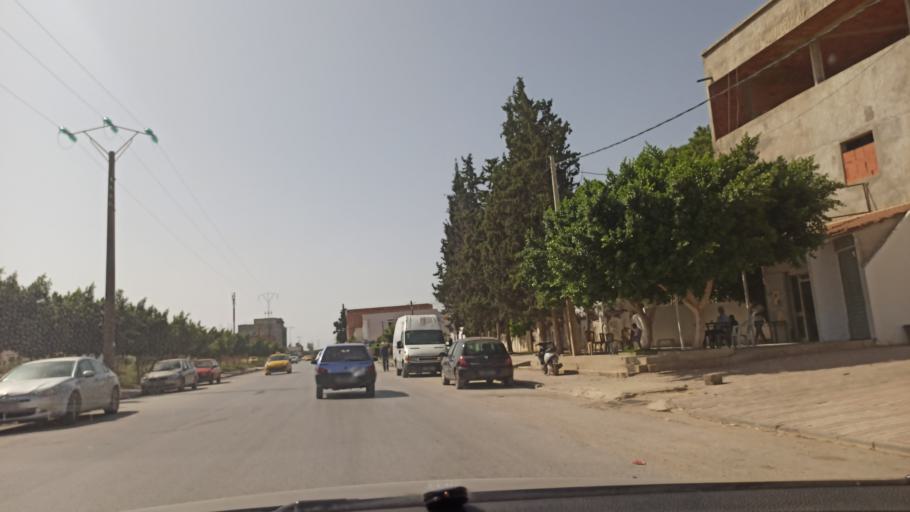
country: TN
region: Manouba
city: Manouba
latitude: 36.7557
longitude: 10.1028
